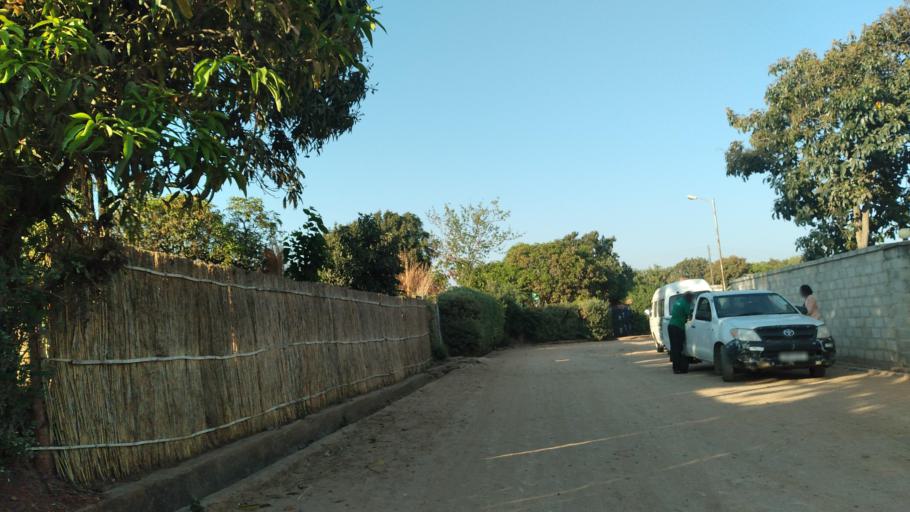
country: ZM
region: Lusaka
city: Lusaka
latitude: -15.5472
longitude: 28.2791
